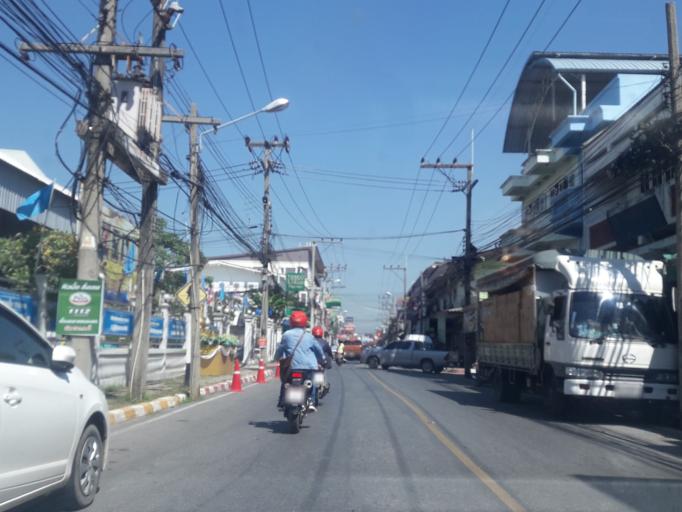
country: TH
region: Sara Buri
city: Nong Khae
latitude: 14.3388
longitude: 100.8668
